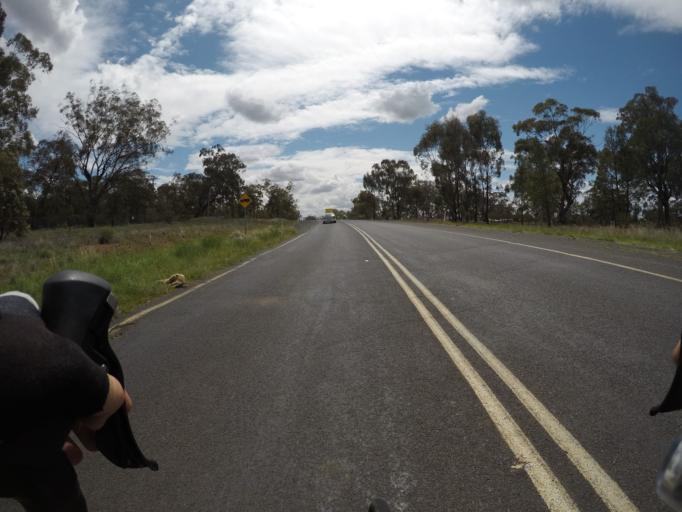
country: AU
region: New South Wales
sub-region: Dubbo Municipality
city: Dubbo
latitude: -32.2862
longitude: 148.5975
